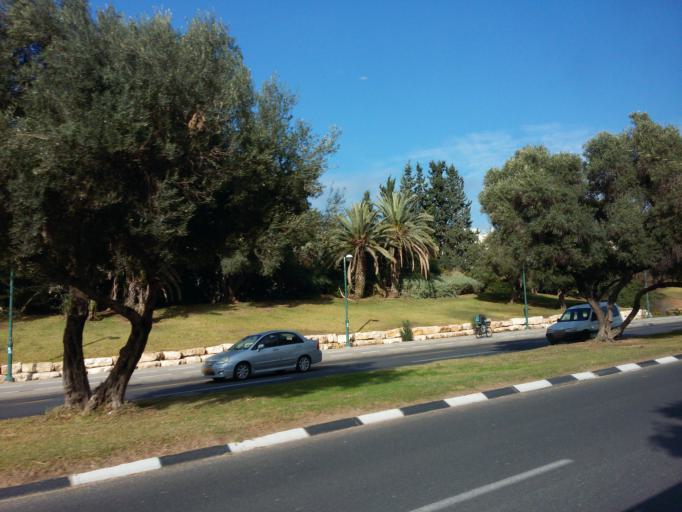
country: IL
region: Tel Aviv
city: Tel Aviv
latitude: 32.1071
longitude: 34.7912
